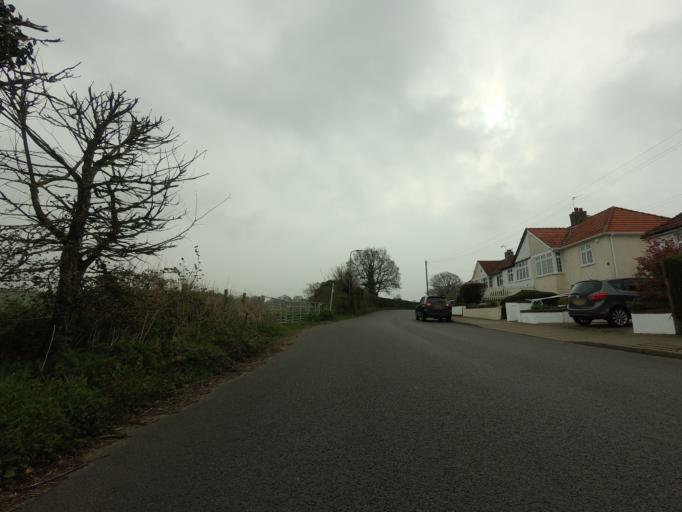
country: GB
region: England
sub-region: Greater London
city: Orpington
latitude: 51.3826
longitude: 0.1216
